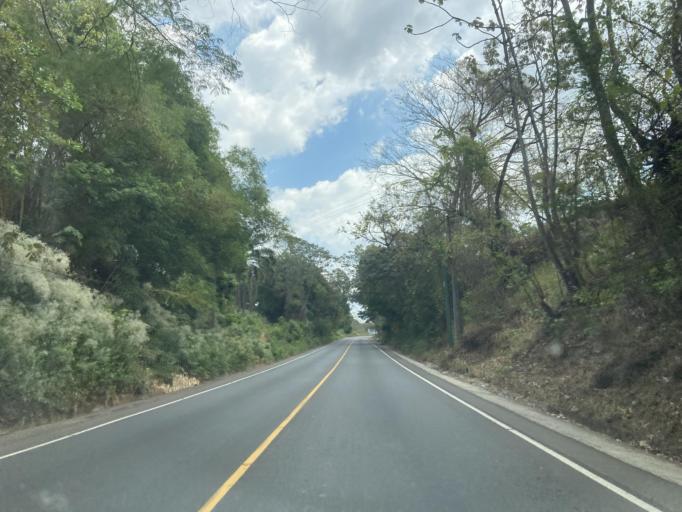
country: GT
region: Santa Rosa
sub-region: Municipio de Taxisco
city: Taxisco
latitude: 14.0893
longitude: -90.5018
